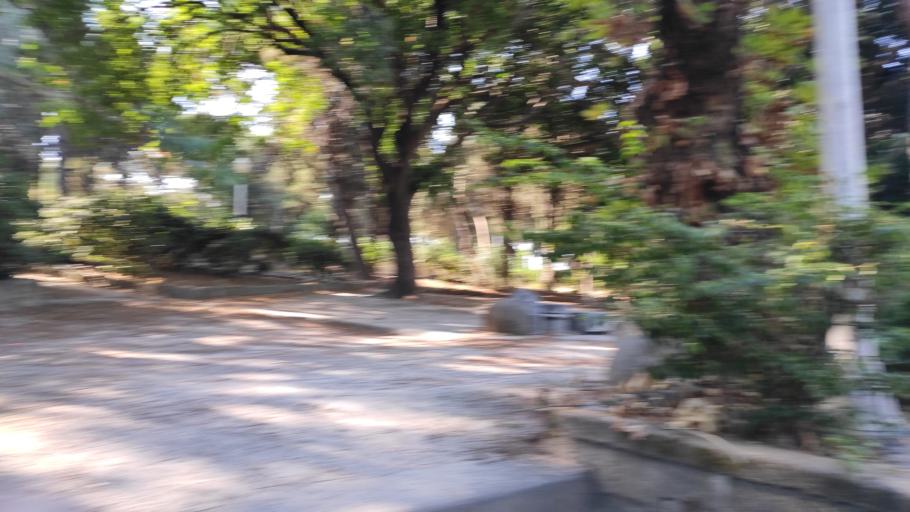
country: GR
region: South Aegean
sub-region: Nomos Dodekanisou
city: Rodos
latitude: 36.4470
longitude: 28.2221
